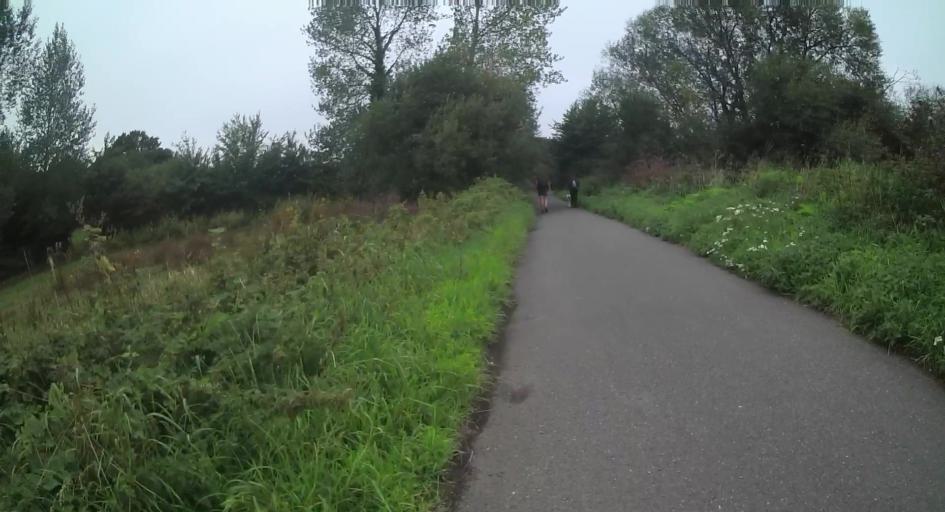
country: GB
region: England
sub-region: Isle of Wight
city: Sandown
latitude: 50.6647
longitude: -1.1772
